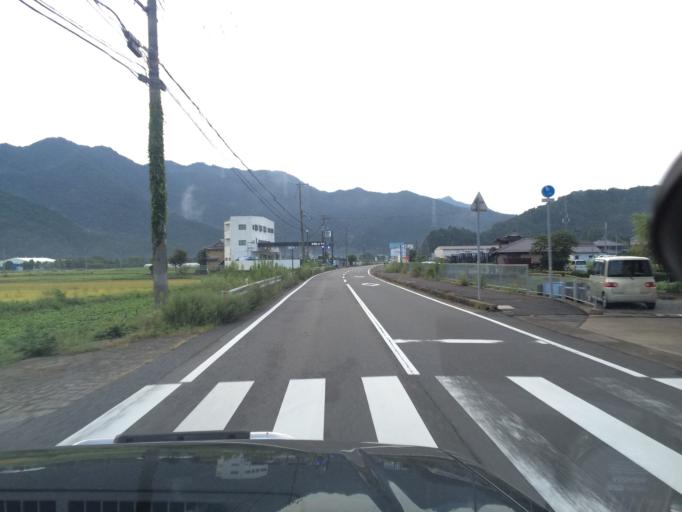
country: JP
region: Hyogo
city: Nishiwaki
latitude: 35.1053
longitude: 134.9945
